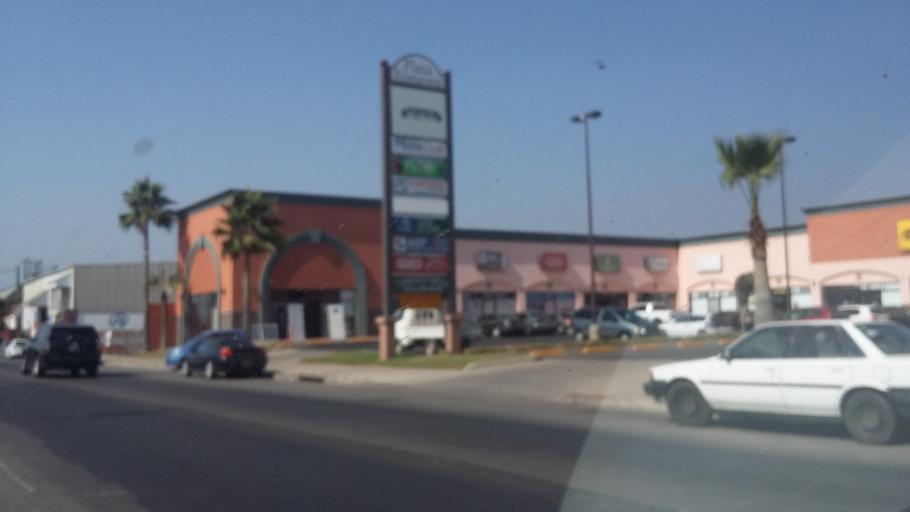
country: MX
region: Baja California
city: Ensenada
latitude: 31.7945
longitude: -116.5935
